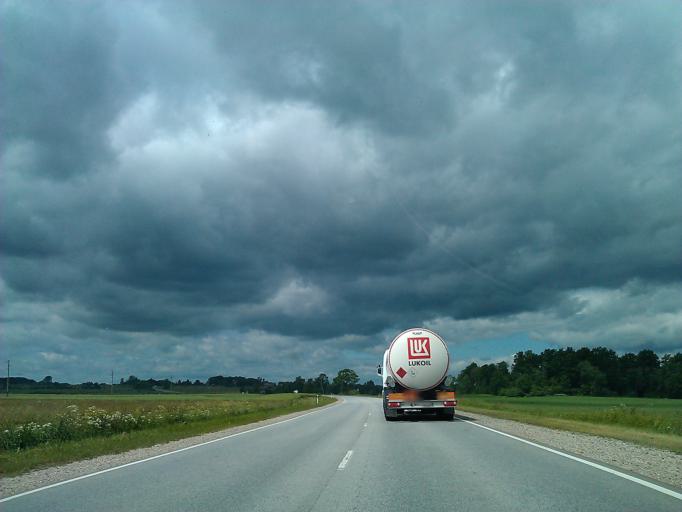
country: LV
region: Engure
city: Smarde
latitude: 56.9211
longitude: 23.2936
